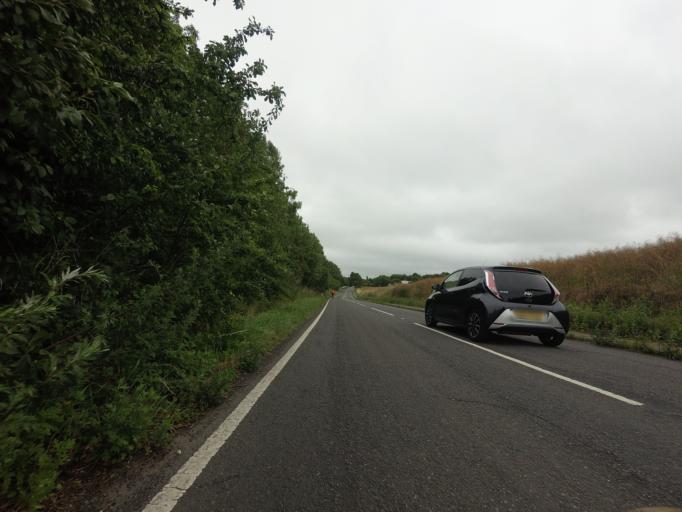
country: GB
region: England
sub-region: Kent
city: Meopham
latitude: 51.3775
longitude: 0.3550
